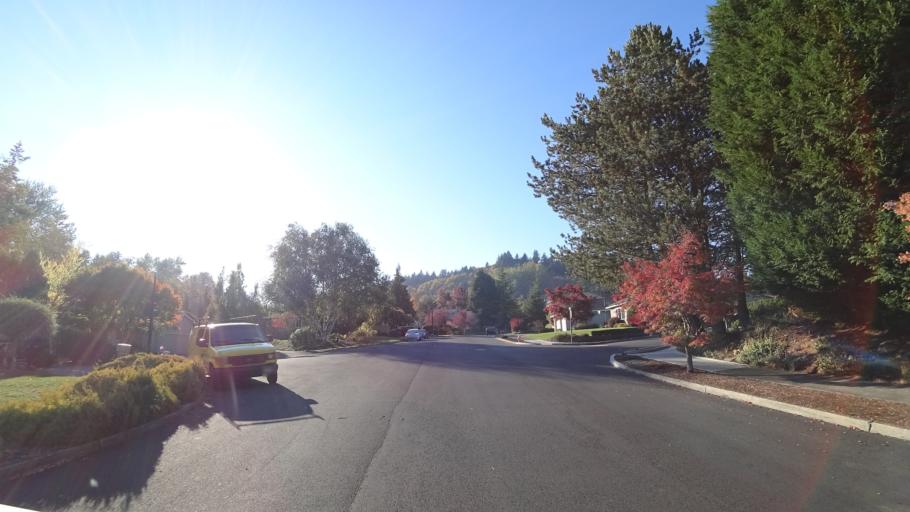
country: US
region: Oregon
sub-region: Multnomah County
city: Gresham
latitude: 45.4861
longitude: -122.4233
